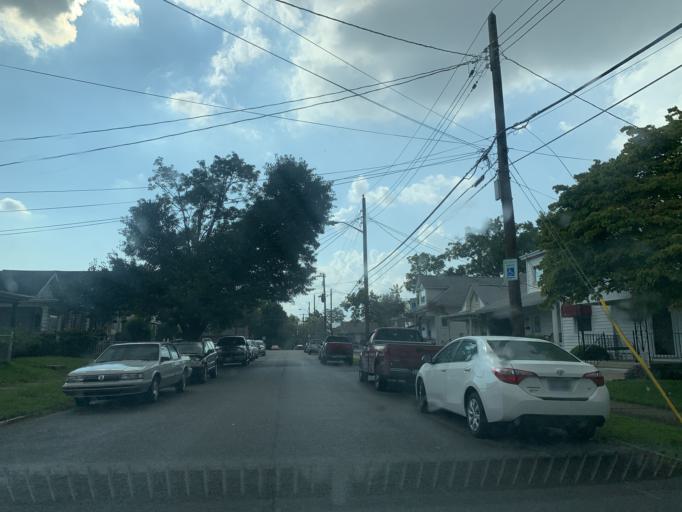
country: US
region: Kentucky
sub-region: Jefferson County
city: Audubon Park
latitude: 38.2154
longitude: -85.7495
